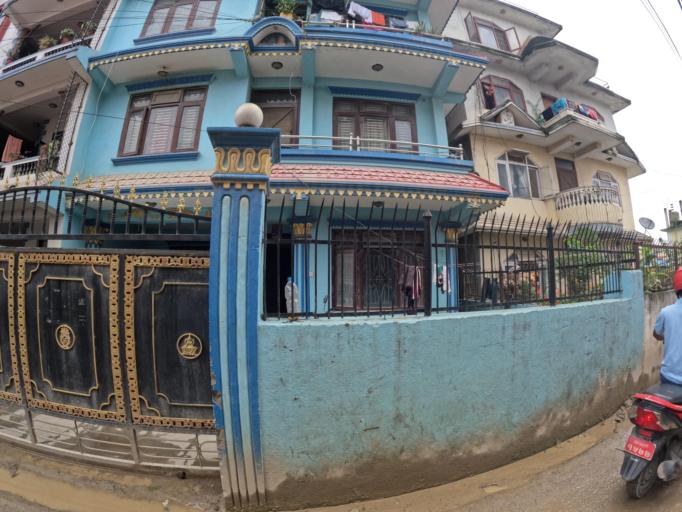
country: NP
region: Central Region
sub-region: Bagmati Zone
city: Kathmandu
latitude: 27.7472
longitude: 85.3212
